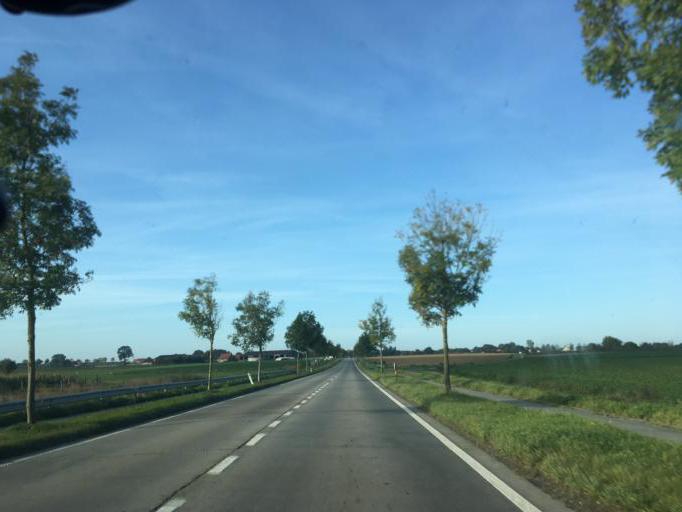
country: BE
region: Flanders
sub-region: Provincie West-Vlaanderen
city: Ieper
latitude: 50.8535
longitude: 2.9294
